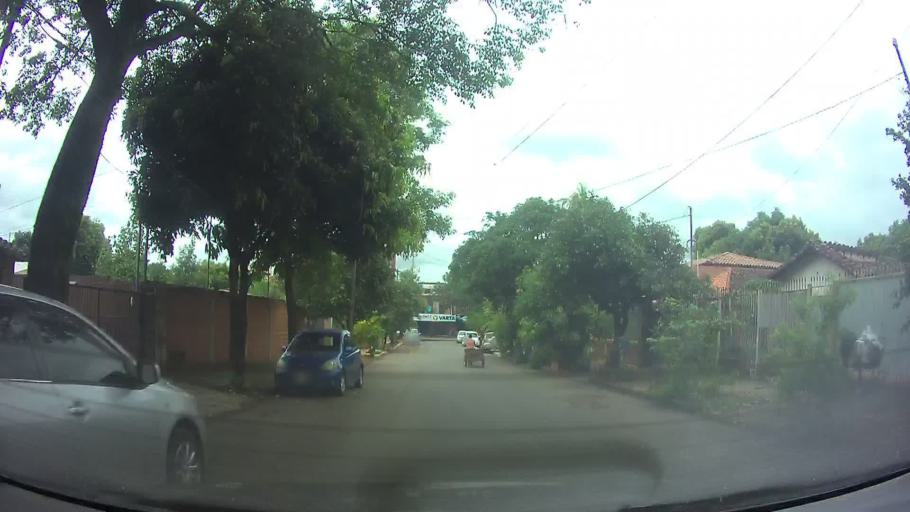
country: PY
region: Central
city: San Lorenzo
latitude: -25.2713
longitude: -57.4836
